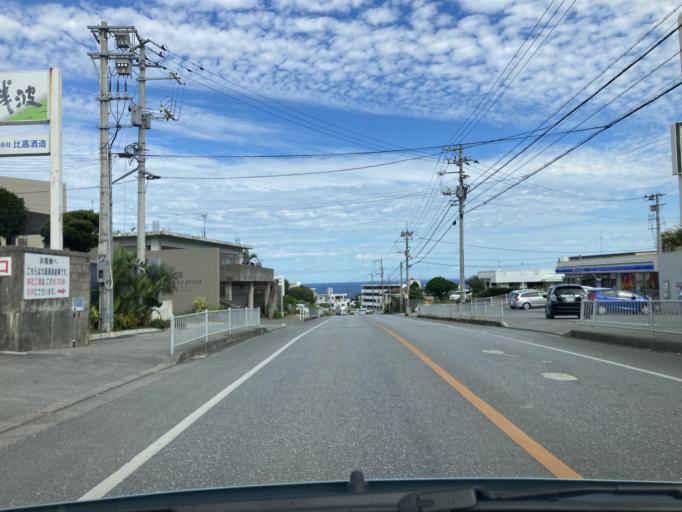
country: JP
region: Okinawa
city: Ishikawa
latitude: 26.4177
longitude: 127.7324
